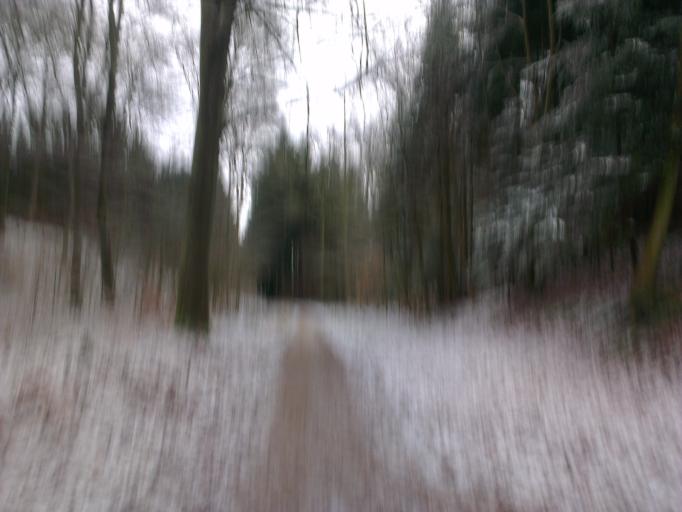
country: DK
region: Capital Region
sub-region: Frederikssund Kommune
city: Frederikssund
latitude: 55.8480
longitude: 12.0241
